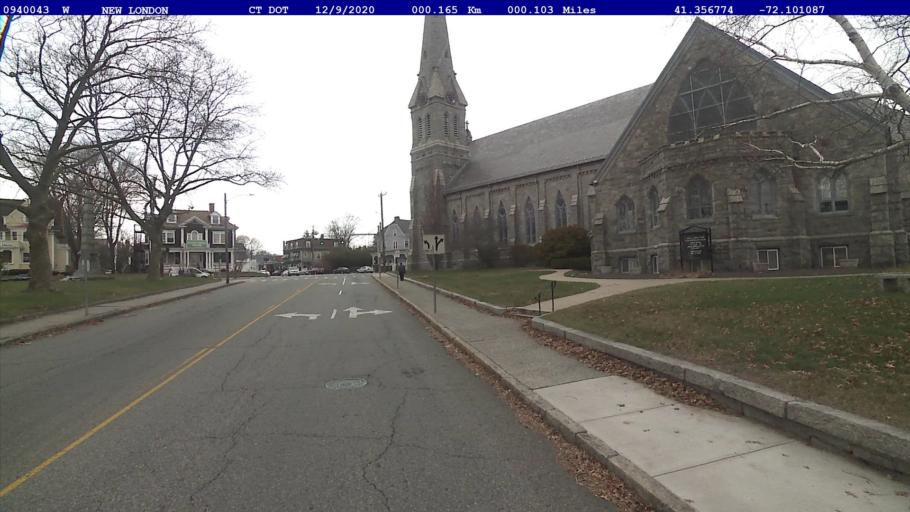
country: US
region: Connecticut
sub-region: New London County
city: New London
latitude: 41.3568
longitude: -72.1011
